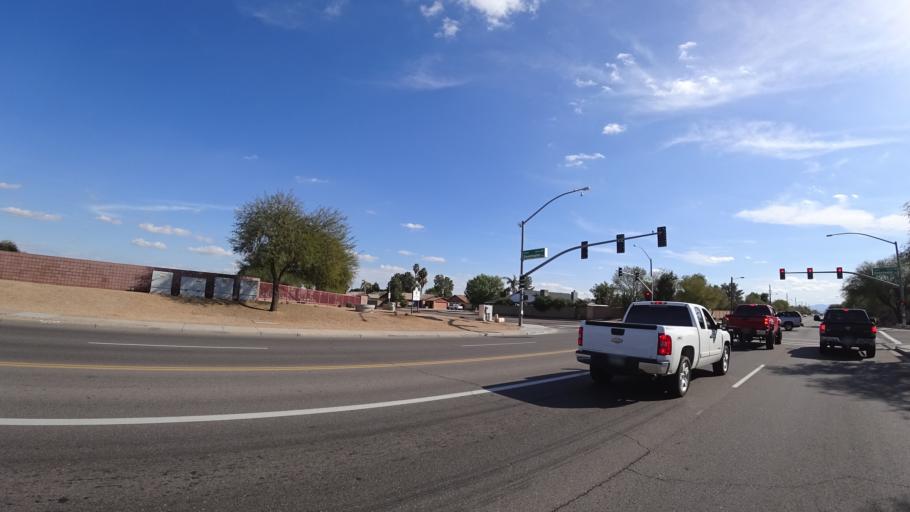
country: US
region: Arizona
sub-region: Maricopa County
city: Peoria
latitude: 33.6035
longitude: -112.2202
